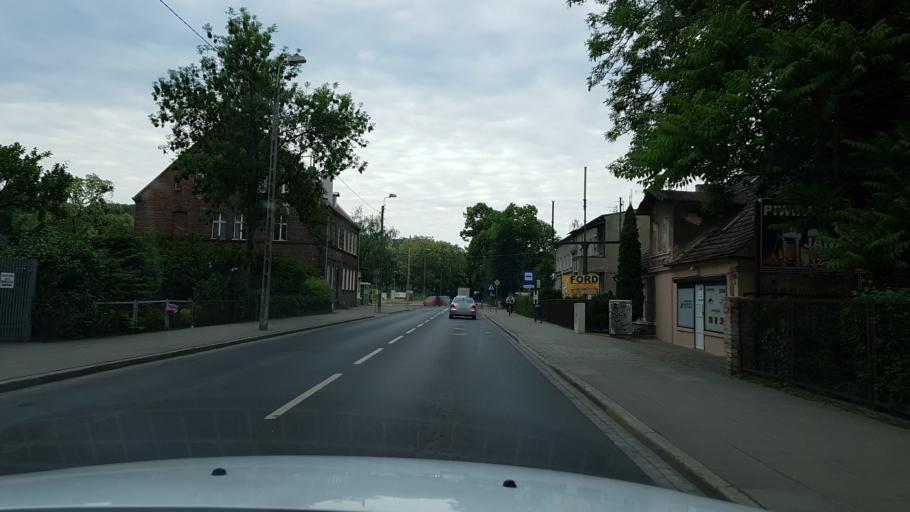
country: PL
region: West Pomeranian Voivodeship
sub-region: Szczecin
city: Szczecin
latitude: 53.3804
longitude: 14.6286
